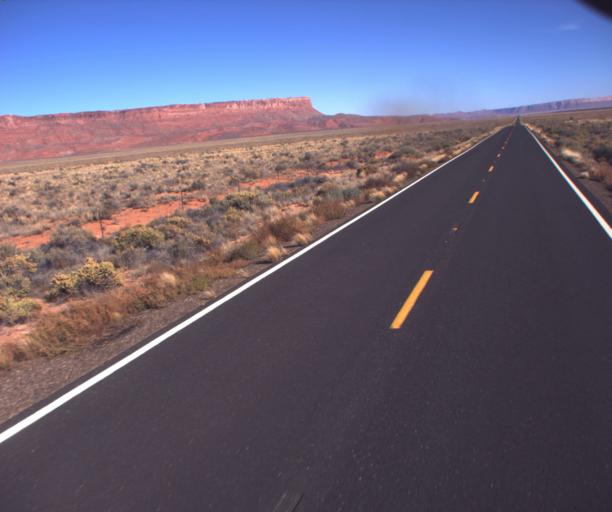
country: US
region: Arizona
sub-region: Coconino County
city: Page
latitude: 36.7064
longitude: -111.9533
